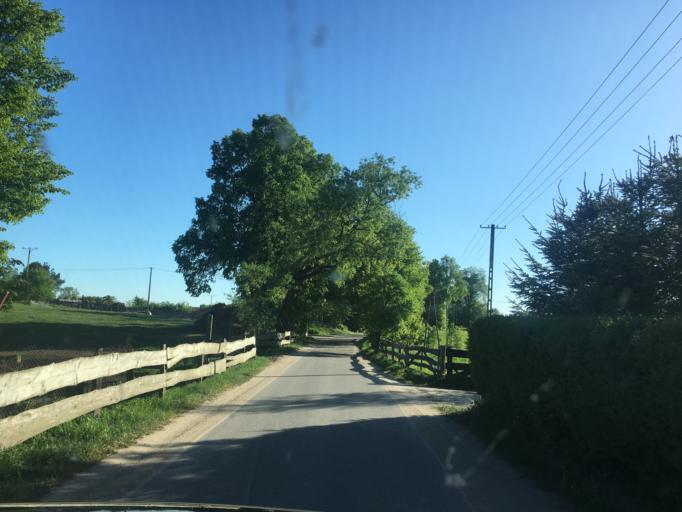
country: PL
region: Warmian-Masurian Voivodeship
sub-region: Powiat piski
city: Ruciane-Nida
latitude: 53.6899
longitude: 21.4781
